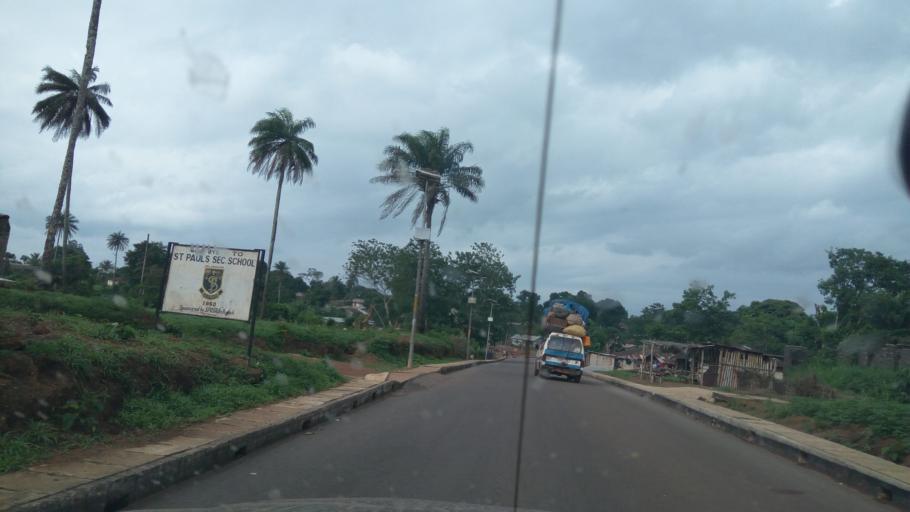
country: SL
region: Southern Province
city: Pujehun
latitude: 7.3595
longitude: -11.7284
